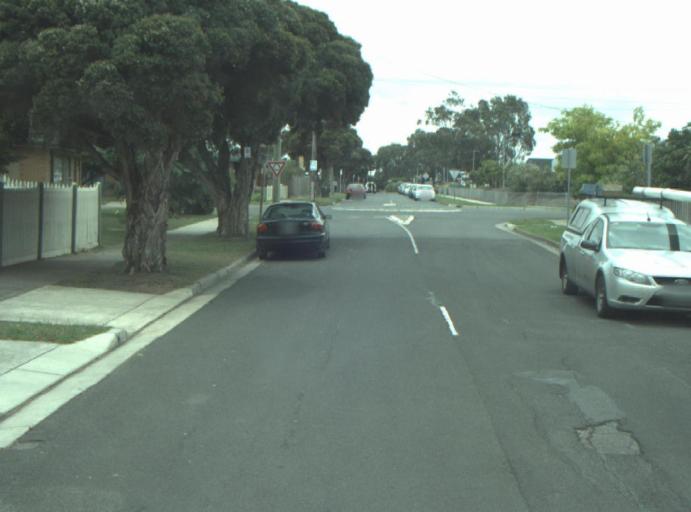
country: AU
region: Victoria
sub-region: Greater Geelong
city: Wandana Heights
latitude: -38.1794
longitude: 144.3267
